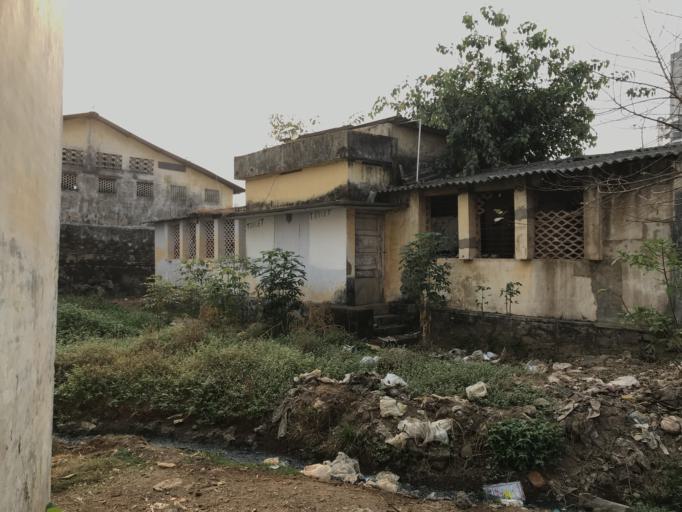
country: IN
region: Kerala
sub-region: Ernakulam
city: Aluva
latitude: 10.1067
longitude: 76.3482
